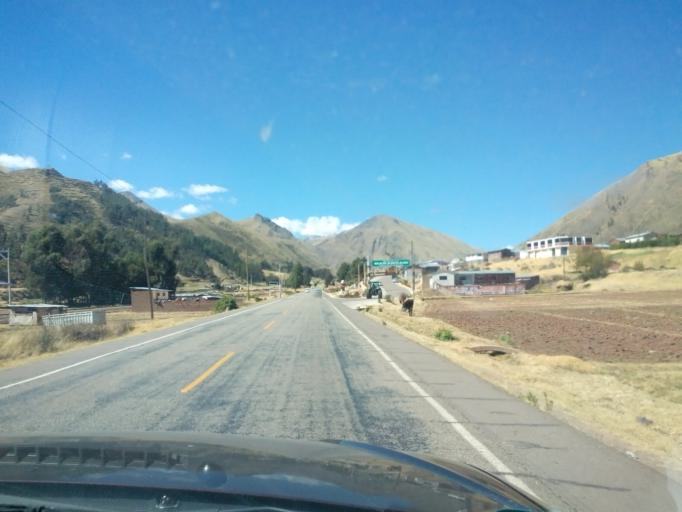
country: PE
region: Cusco
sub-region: Provincia de Canchis
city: Marangani
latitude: -14.3514
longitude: -71.1742
